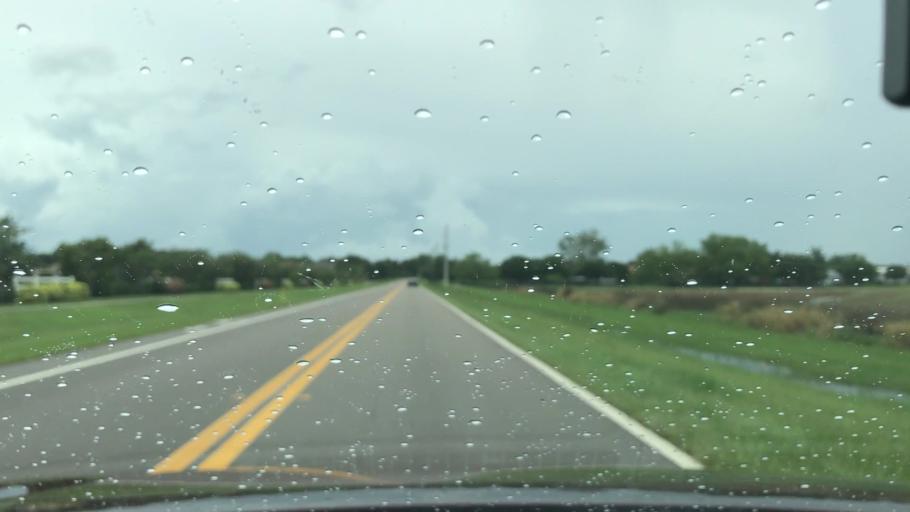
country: US
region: Florida
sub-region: Sarasota County
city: Lake Sarasota
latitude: 27.3140
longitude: -82.3964
